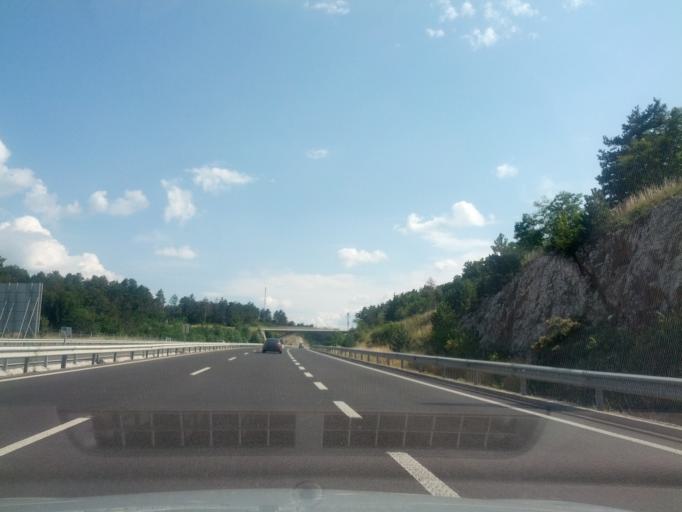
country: SI
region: Hrpelje-Kozina
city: Kozina
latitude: 45.6418
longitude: 13.9608
